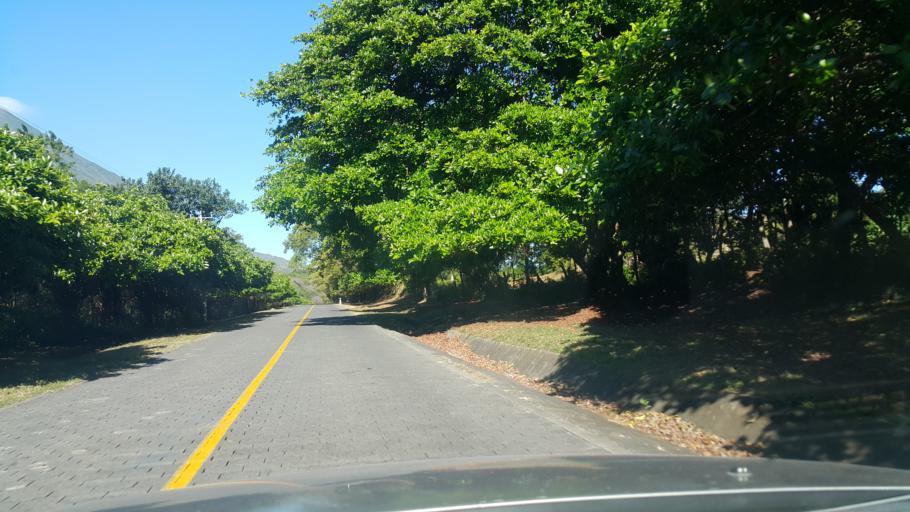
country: NI
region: Rivas
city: Moyogalpa
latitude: 11.4890
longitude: -85.6312
